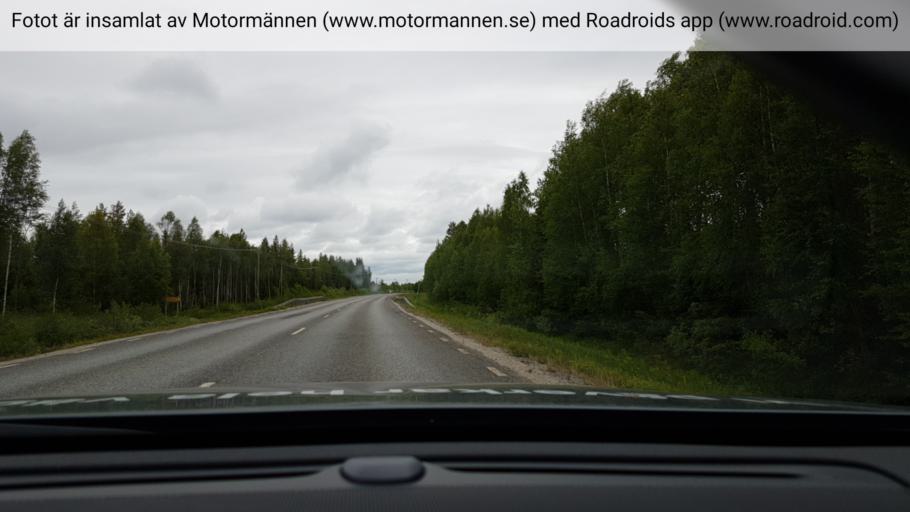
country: SE
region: Vaesterbotten
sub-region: Lycksele Kommun
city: Lycksele
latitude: 64.5564
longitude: 18.5168
